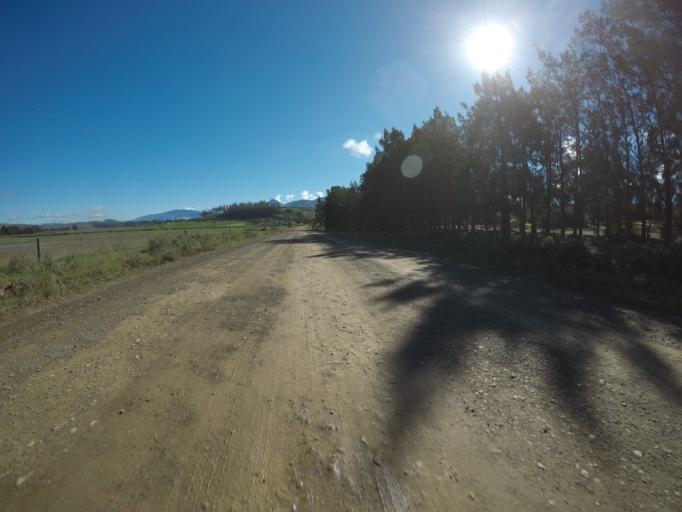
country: ZA
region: Western Cape
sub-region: Overberg District Municipality
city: Caledon
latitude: -34.1001
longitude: 19.6996
